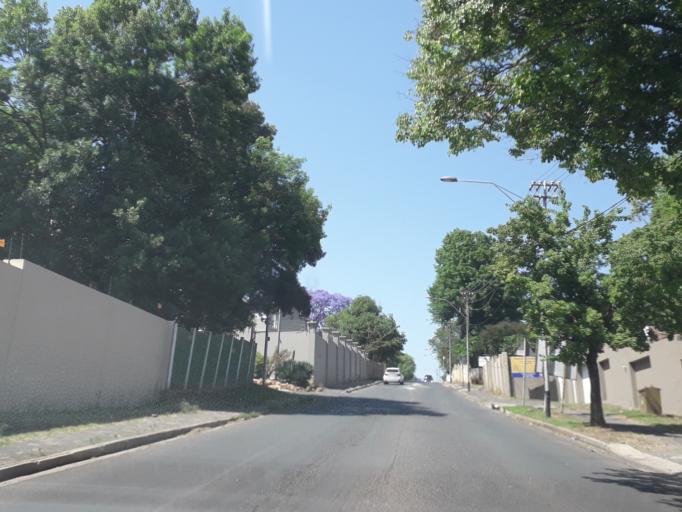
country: ZA
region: Gauteng
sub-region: City of Johannesburg Metropolitan Municipality
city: Johannesburg
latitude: -26.1336
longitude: 28.0249
